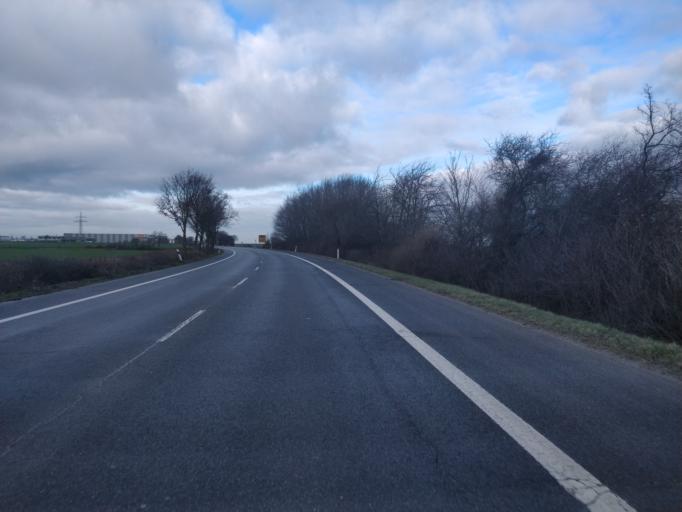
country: DE
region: North Rhine-Westphalia
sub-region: Regierungsbezirk Koln
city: Euskirchen
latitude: 50.6804
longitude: 6.8452
